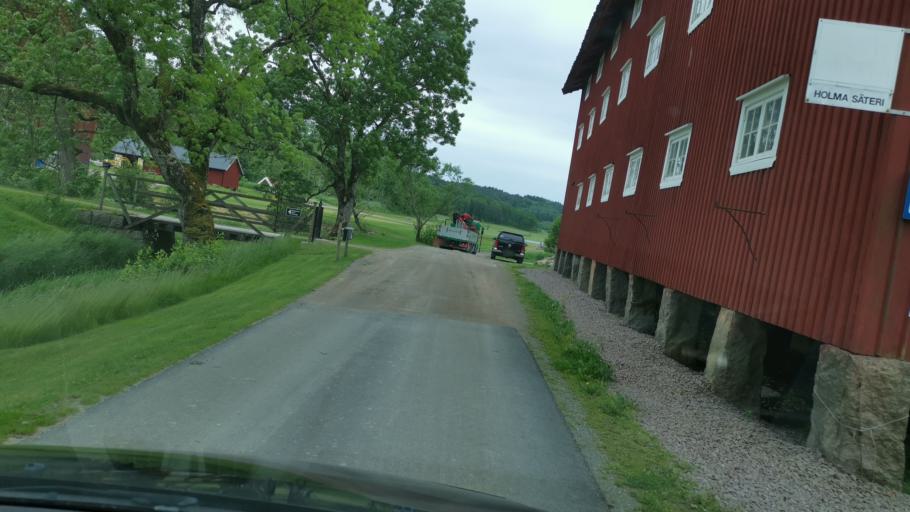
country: SE
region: Vaestra Goetaland
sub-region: Lysekils Kommun
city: Brastad
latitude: 58.3760
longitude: 11.5525
